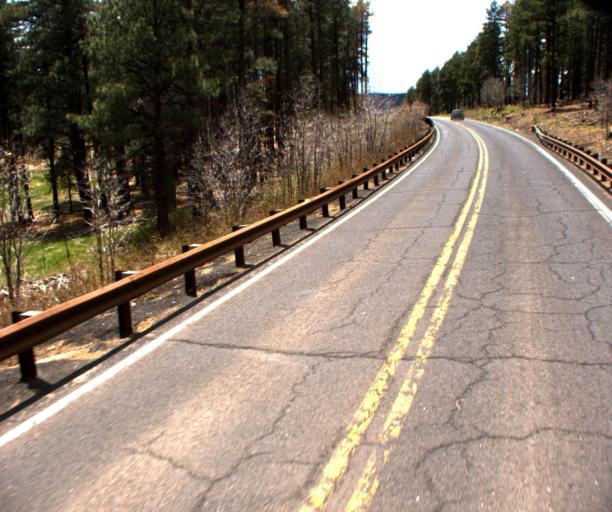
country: US
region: Arizona
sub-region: Coconino County
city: Kachina Village
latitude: 35.1085
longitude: -111.7222
